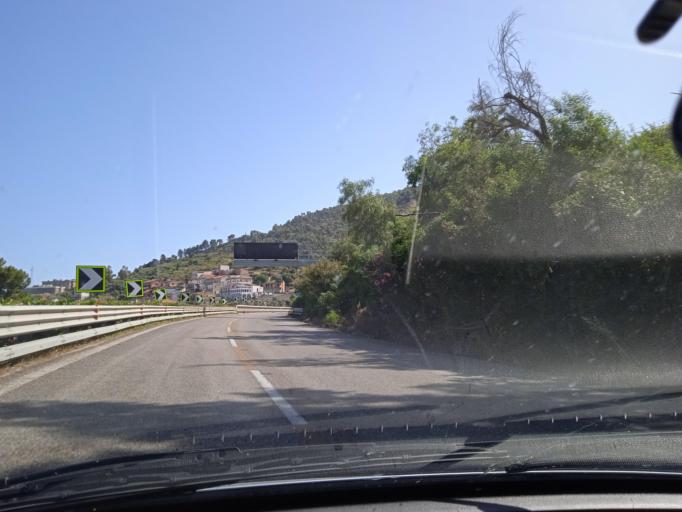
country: IT
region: Sicily
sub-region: Messina
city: Capo d'Orlando
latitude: 38.1350
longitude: 14.7379
